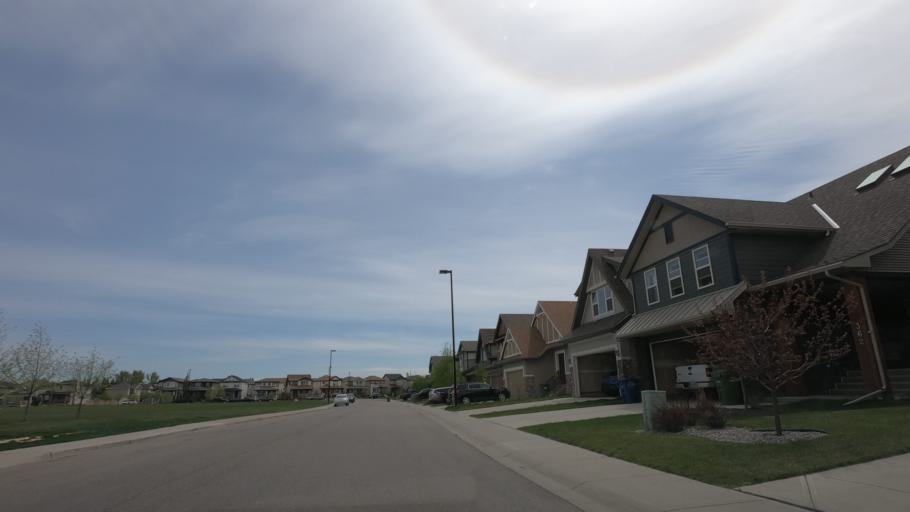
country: CA
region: Alberta
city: Airdrie
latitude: 51.3044
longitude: -114.0401
